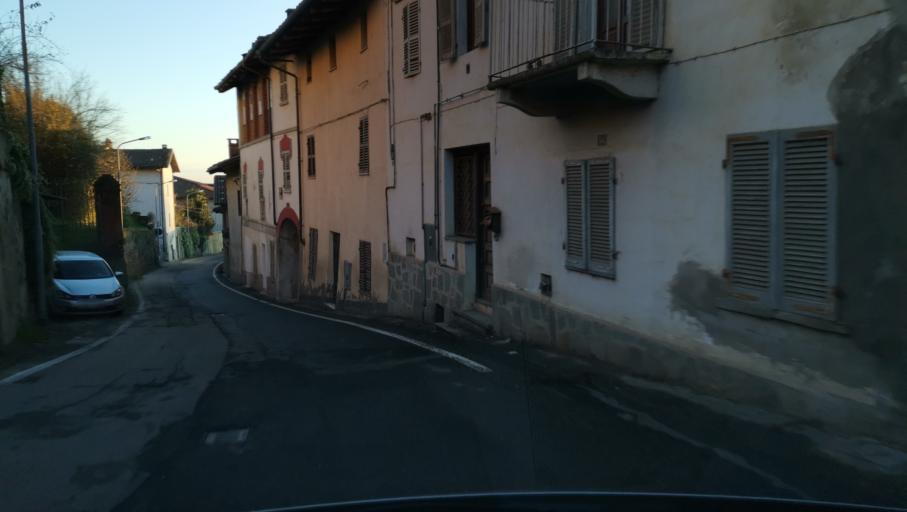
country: IT
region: Piedmont
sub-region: Provincia di Asti
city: Moncucco Torinese
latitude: 45.0662
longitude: 7.9332
